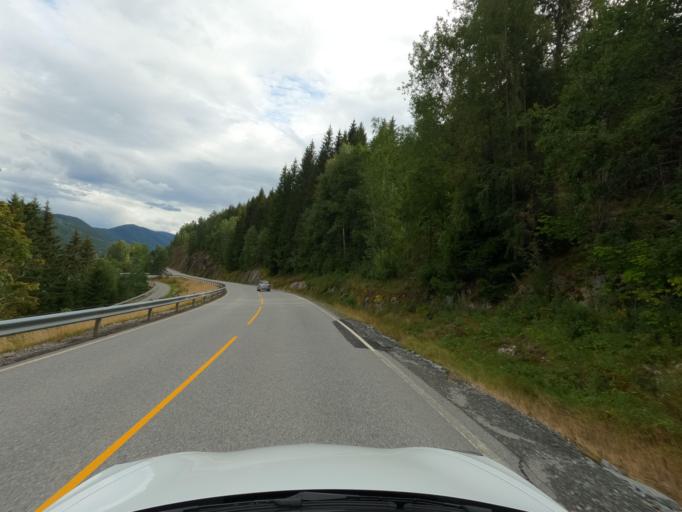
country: NO
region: Telemark
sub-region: Hjartdal
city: Sauland
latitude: 59.8080
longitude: 8.9906
